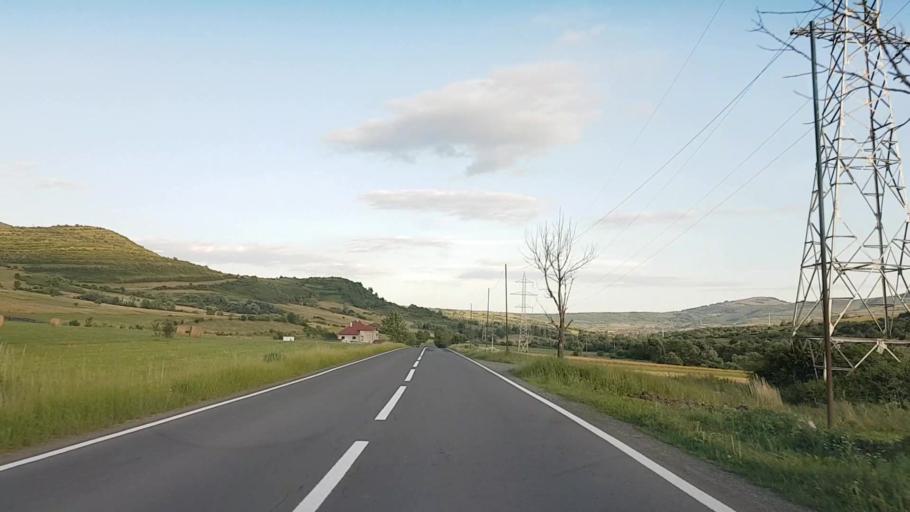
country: RO
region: Harghita
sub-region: Comuna Praid
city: Ocna de Sus
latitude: 46.5129
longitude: 25.1563
